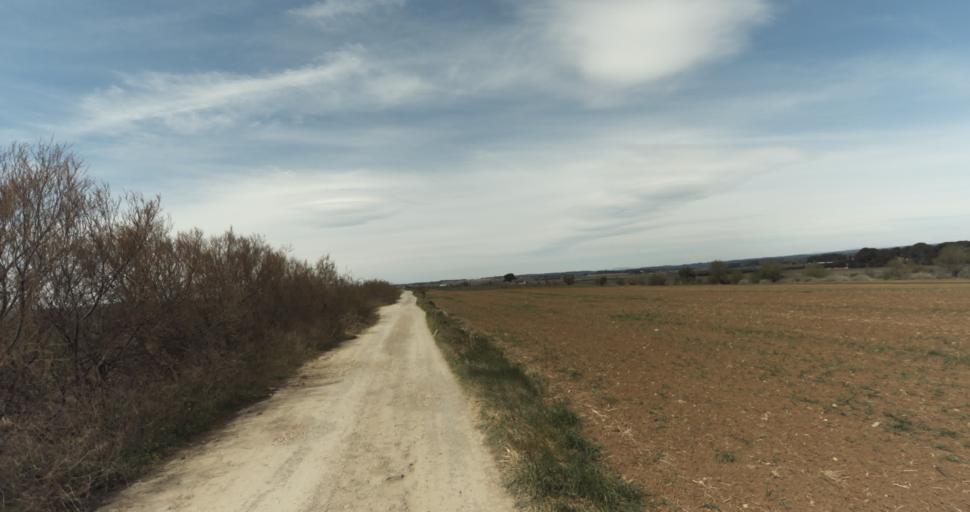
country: FR
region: Languedoc-Roussillon
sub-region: Departement de l'Herault
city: Meze
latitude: 43.4000
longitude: 3.5625
